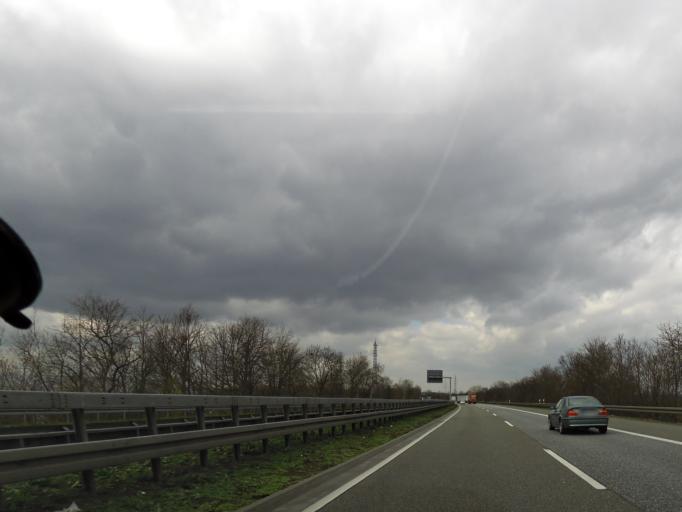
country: DE
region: North Rhine-Westphalia
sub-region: Regierungsbezirk Koln
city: Rheinbach
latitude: 50.6315
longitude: 6.9685
